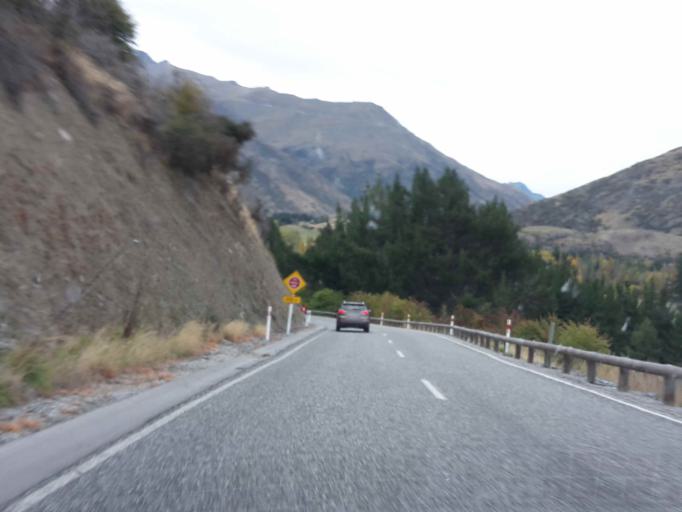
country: NZ
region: Otago
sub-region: Queenstown-Lakes District
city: Arrowtown
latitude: -44.9800
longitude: 168.8567
